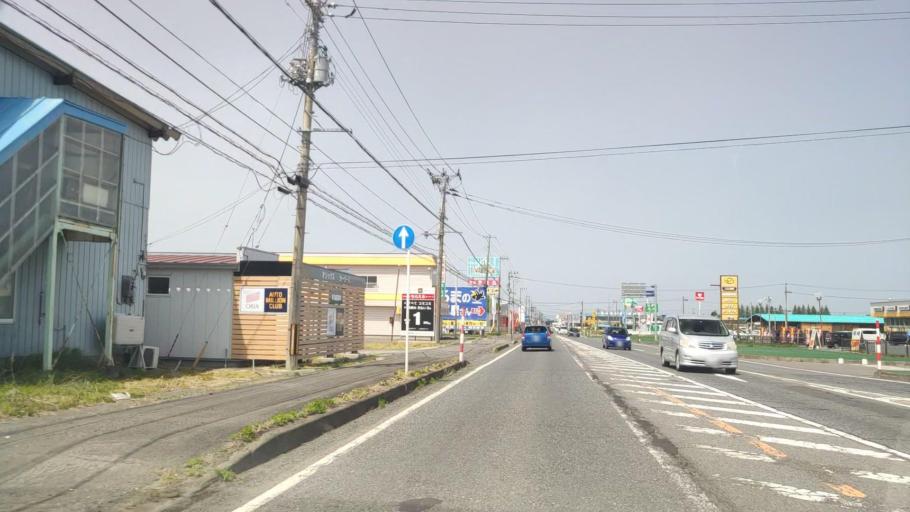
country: JP
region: Aomori
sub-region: Misawa Shi
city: Inuotose
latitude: 40.6447
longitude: 141.1987
